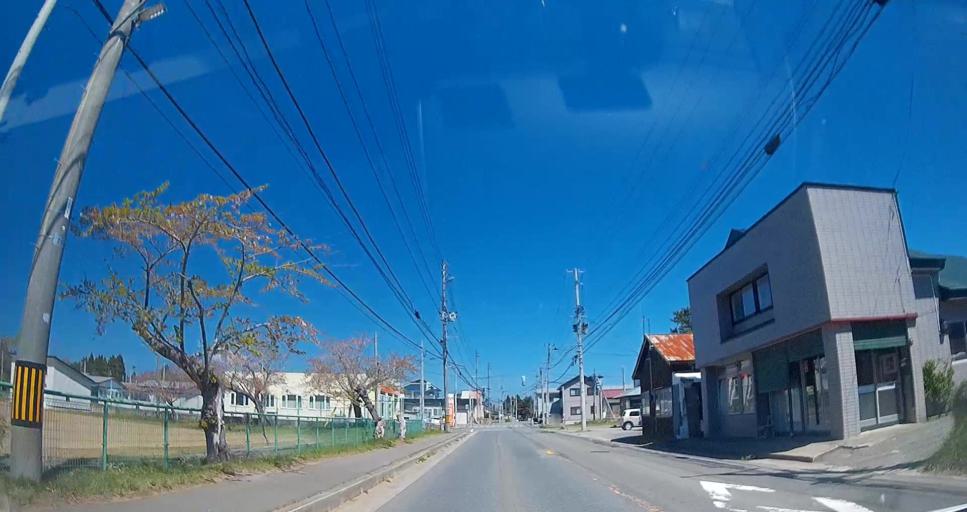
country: JP
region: Aomori
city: Misawa
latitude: 40.9680
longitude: 141.3749
